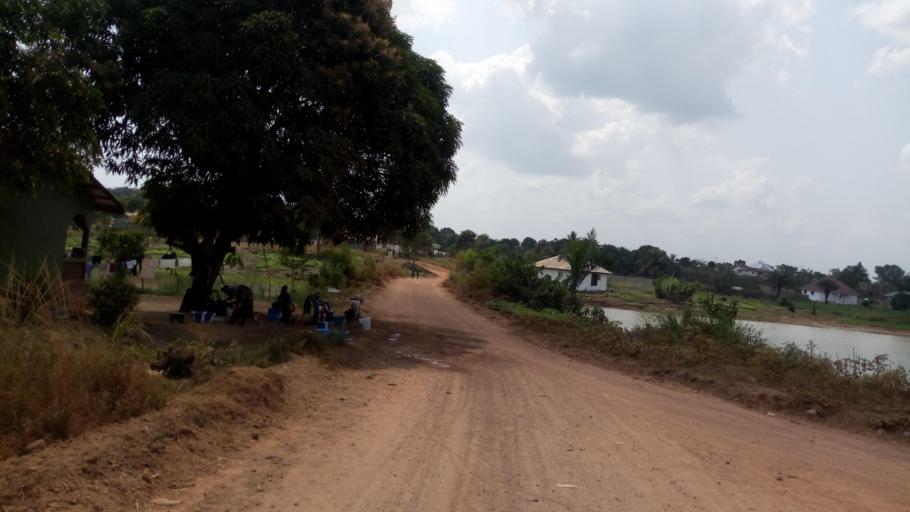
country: SL
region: Southern Province
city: Mogbwemo
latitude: 7.7941
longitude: -12.3008
